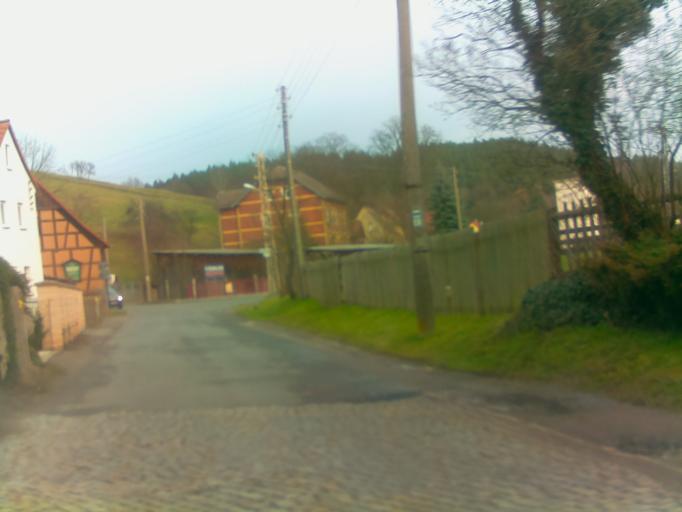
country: DE
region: Thuringia
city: Unterbodnitz
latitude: 50.8216
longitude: 11.6507
